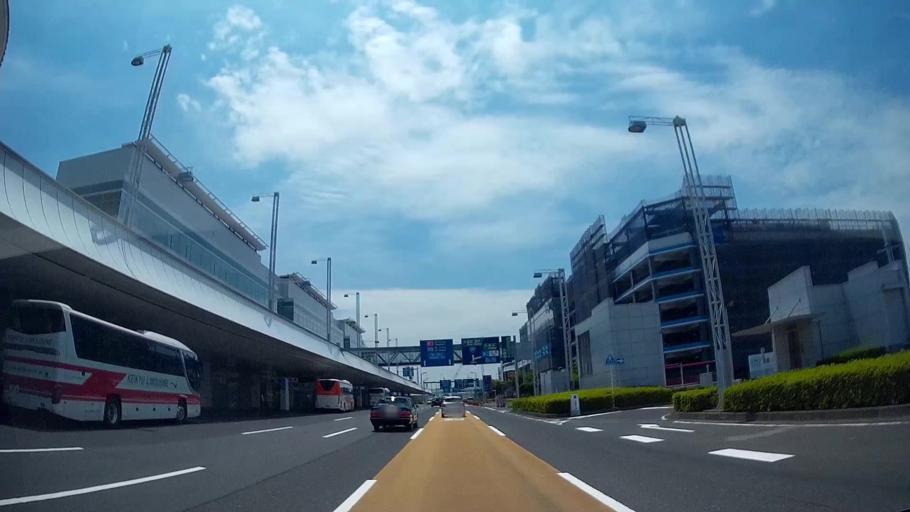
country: JP
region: Kanagawa
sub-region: Kawasaki-shi
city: Kawasaki
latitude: 35.5500
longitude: 139.7885
